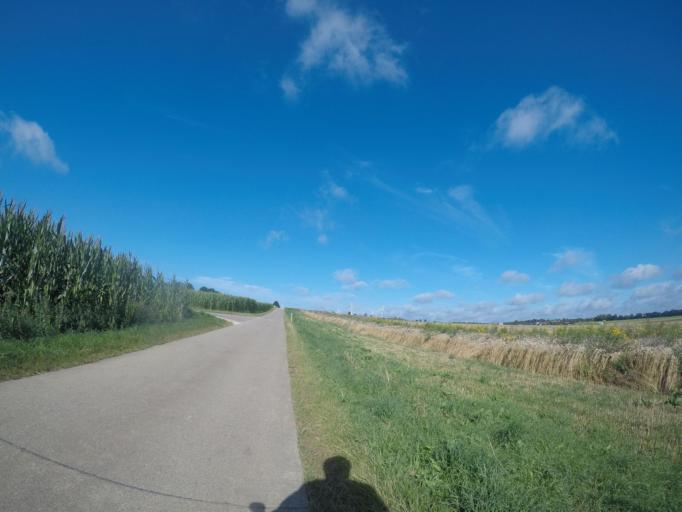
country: DE
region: Baden-Wuerttemberg
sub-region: Tuebingen Region
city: Schelklingen
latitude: 48.3871
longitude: 9.6503
